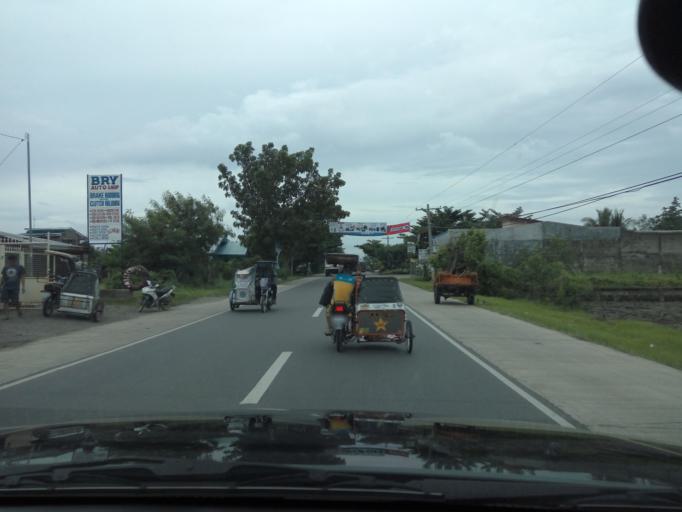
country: PH
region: Central Luzon
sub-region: Province of Nueva Ecija
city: Carmen
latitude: 15.4471
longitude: 120.8179
